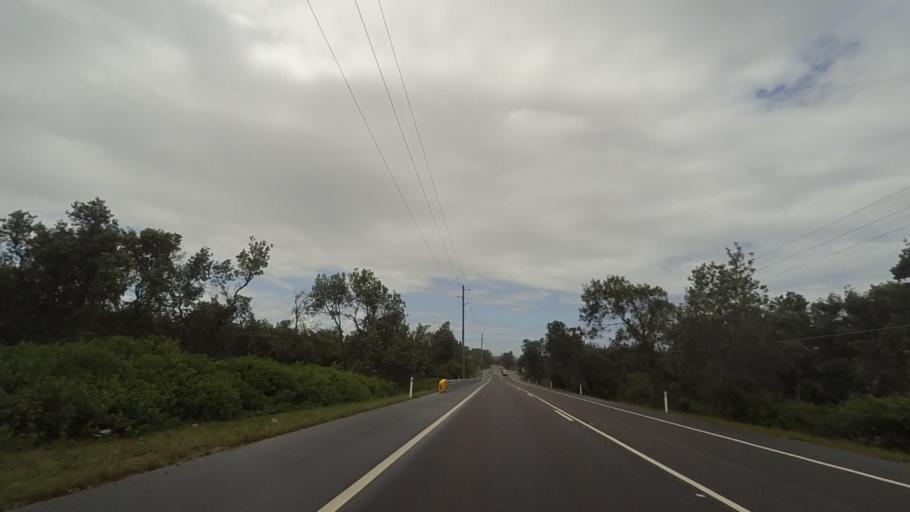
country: AU
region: New South Wales
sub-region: Wyong Shire
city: The Entrance
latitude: -33.3217
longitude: 151.5147
